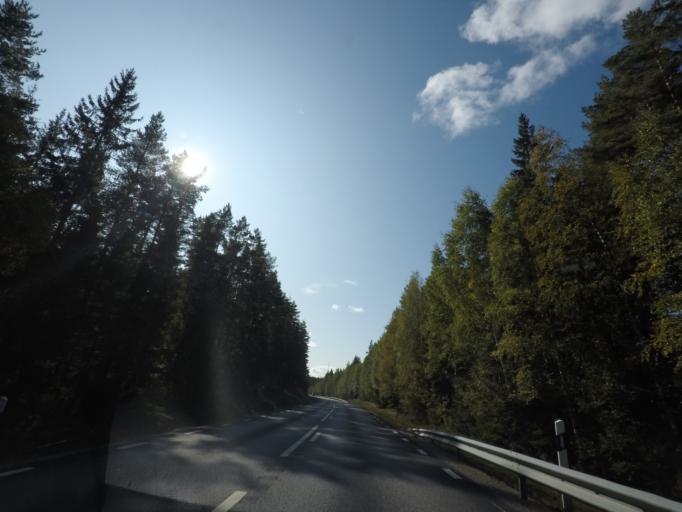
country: SE
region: Vaestmanland
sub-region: Skinnskattebergs Kommun
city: Skinnskatteberg
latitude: 59.8636
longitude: 15.5979
